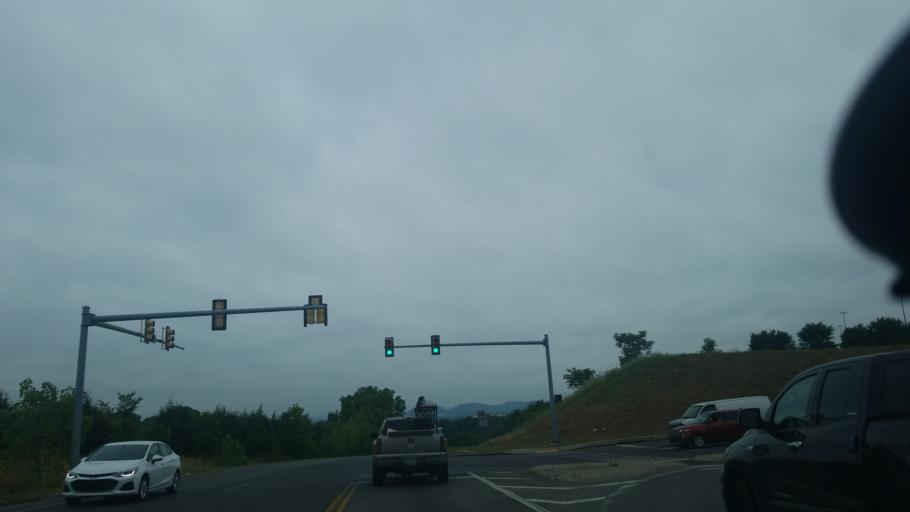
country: US
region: Tennessee
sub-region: Davidson County
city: Nashville
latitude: 36.2424
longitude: -86.7598
